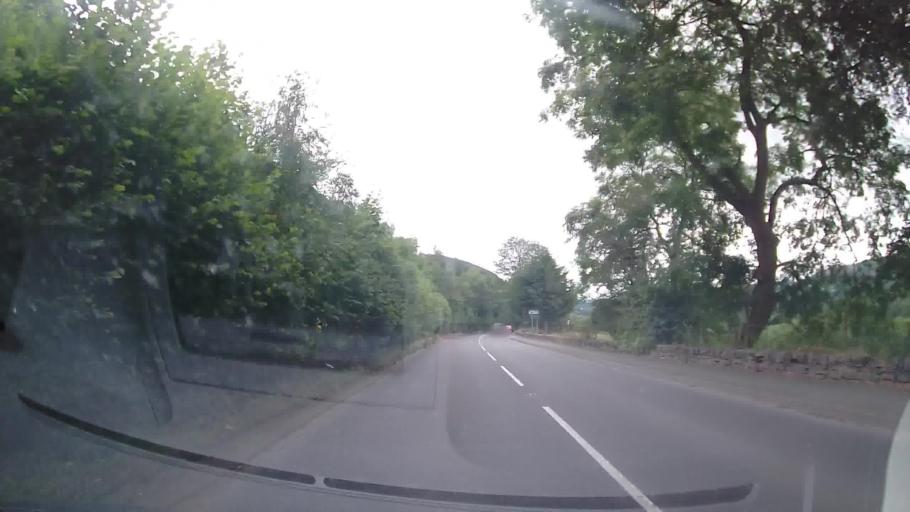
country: GB
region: Wales
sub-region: Wrexham
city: Chirk
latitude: 52.9607
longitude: -3.1064
